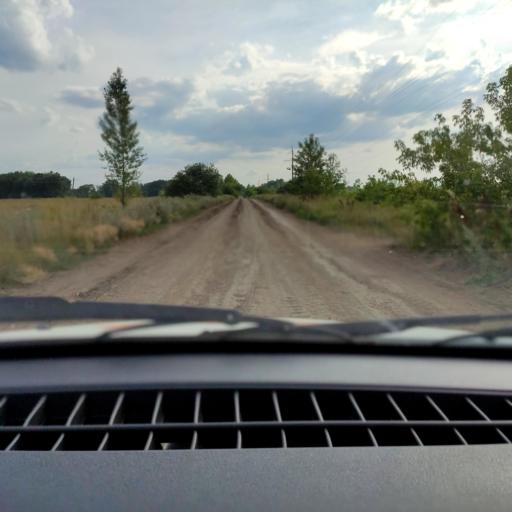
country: RU
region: Bashkortostan
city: Blagoveshchensk
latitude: 54.9249
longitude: 55.9436
